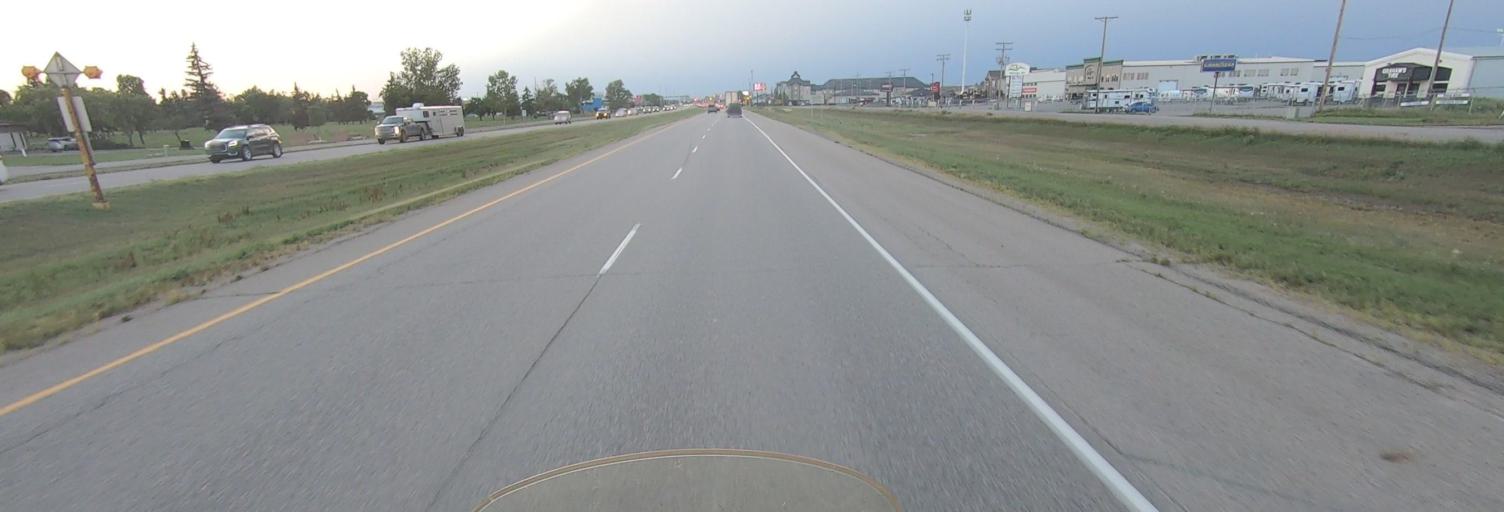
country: CA
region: Saskatchewan
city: Regina
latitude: 50.4477
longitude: -104.5198
